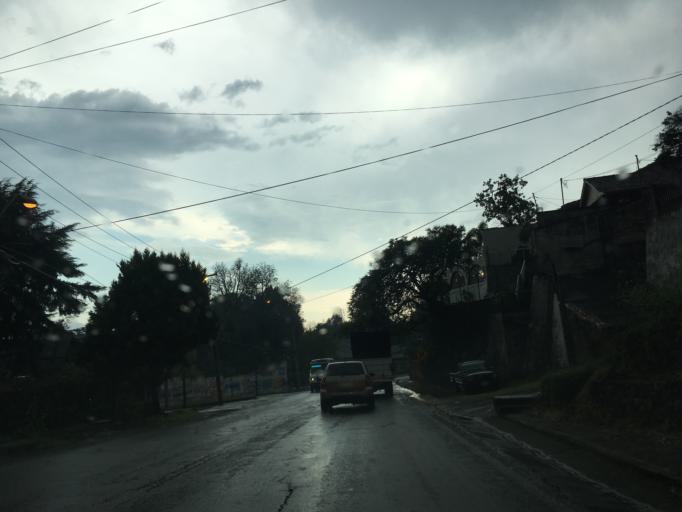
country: MX
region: Michoacan
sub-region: Uruapan
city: Uruapan
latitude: 19.4304
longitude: -102.0724
